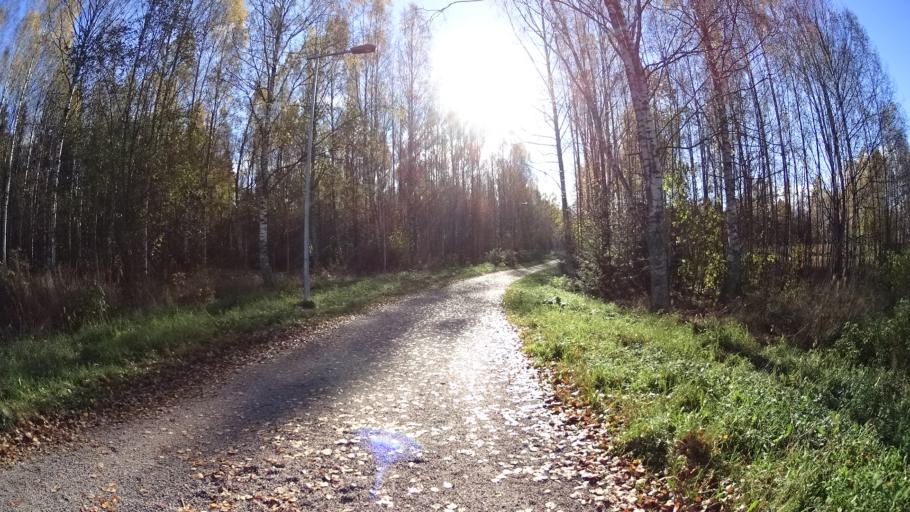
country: FI
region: Uusimaa
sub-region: Helsinki
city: Kilo
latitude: 60.2416
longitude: 24.7973
